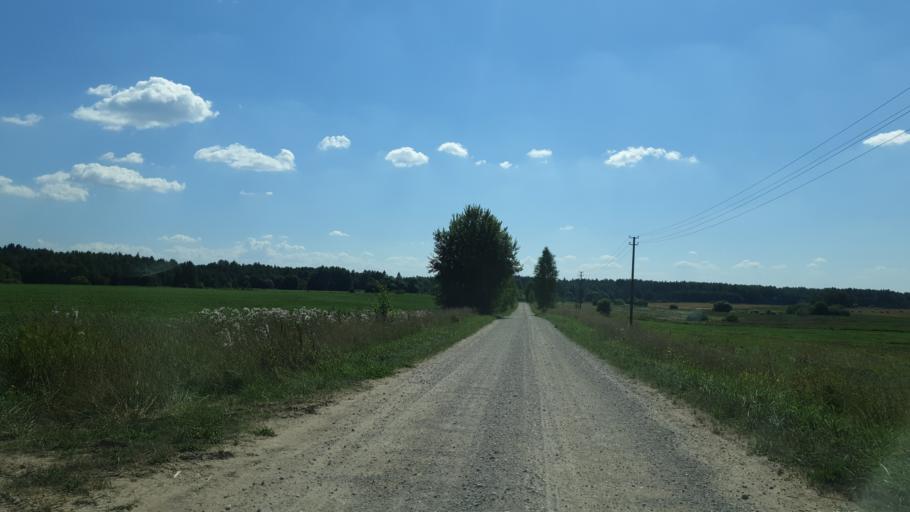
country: LT
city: Sirvintos
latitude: 54.9076
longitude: 24.9113
